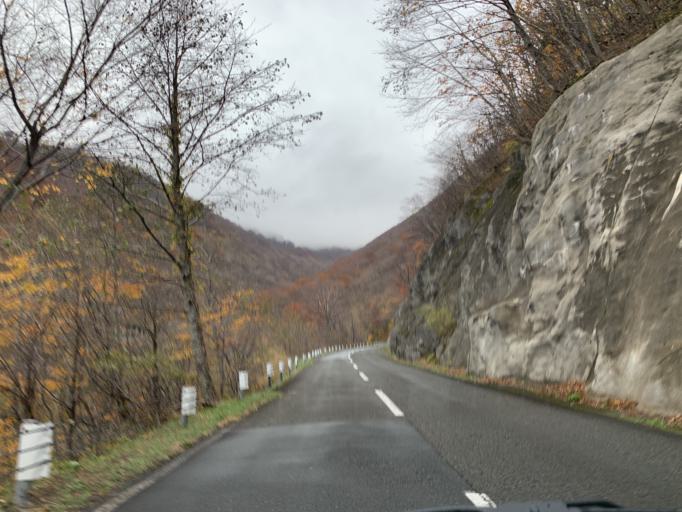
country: JP
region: Iwate
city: Mizusawa
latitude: 39.1200
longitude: 140.8323
